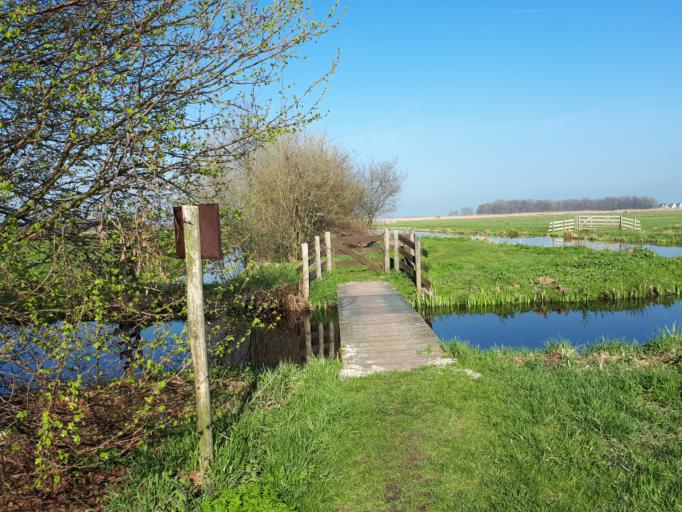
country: NL
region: South Holland
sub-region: Molenwaard
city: Nieuw-Lekkerland
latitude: 51.9472
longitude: 4.6837
